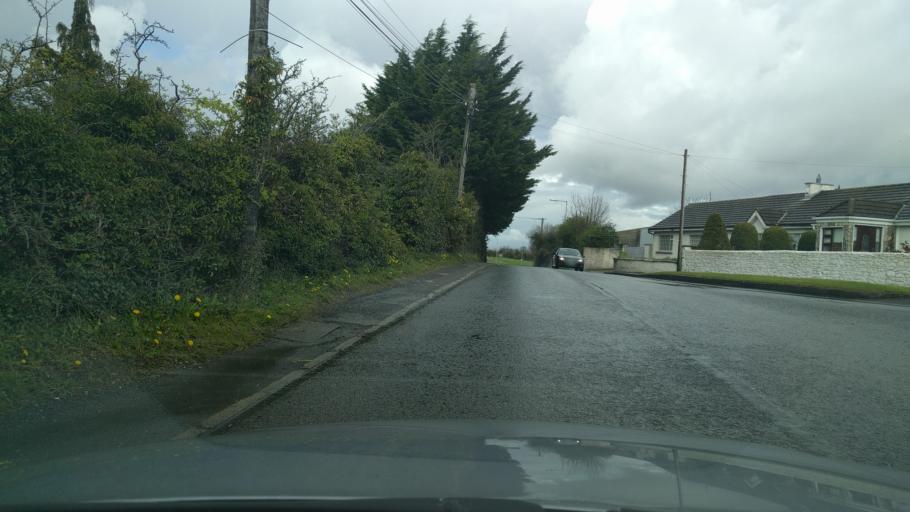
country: IE
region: Leinster
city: Oldbawn
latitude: 53.2713
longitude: -6.3579
